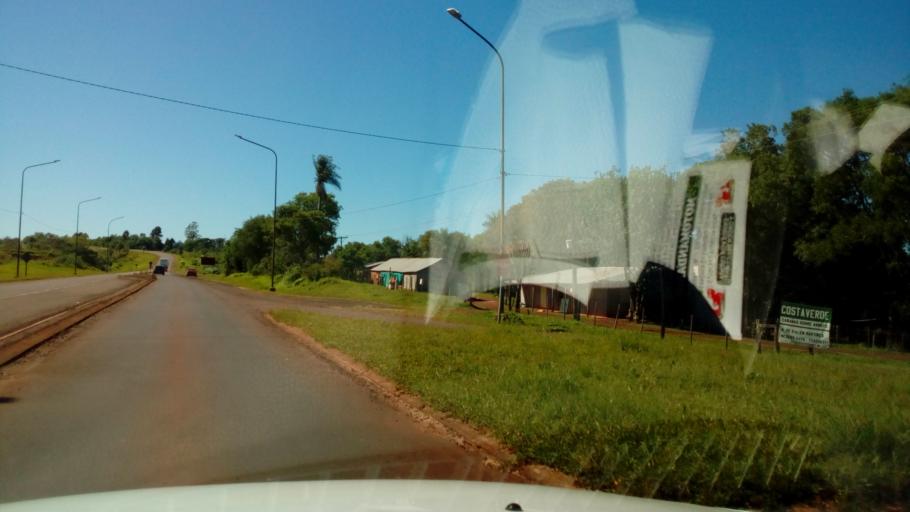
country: AR
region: Misiones
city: Santa Ana
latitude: -27.4051
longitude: -55.5548
